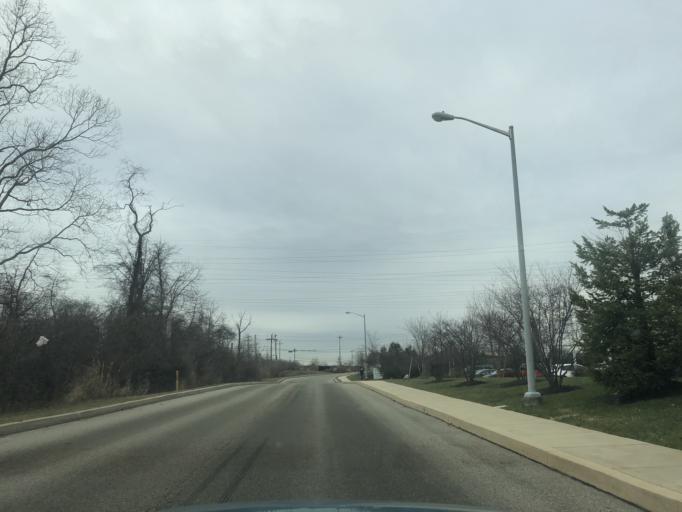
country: US
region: Pennsylvania
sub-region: Montgomery County
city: Plymouth Meeting
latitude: 40.1067
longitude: -75.2970
